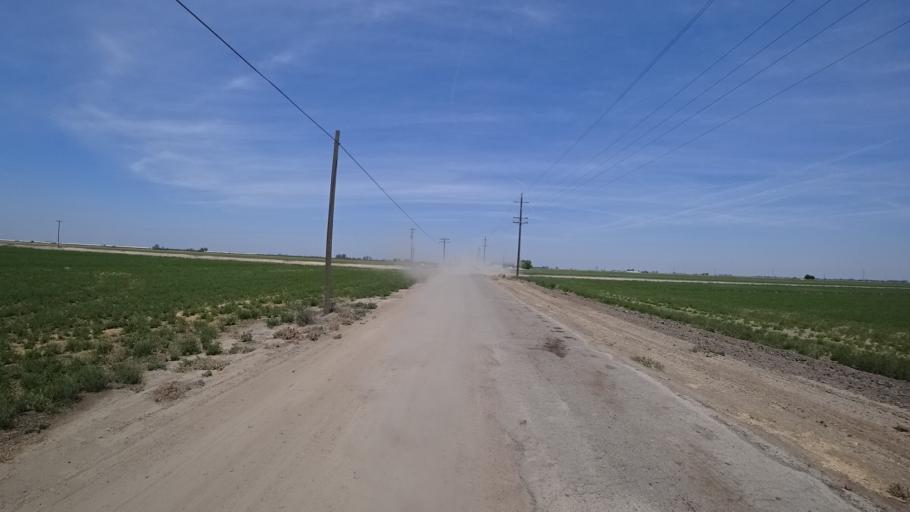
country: US
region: California
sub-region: Fresno County
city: Riverdale
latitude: 36.4009
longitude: -119.9052
